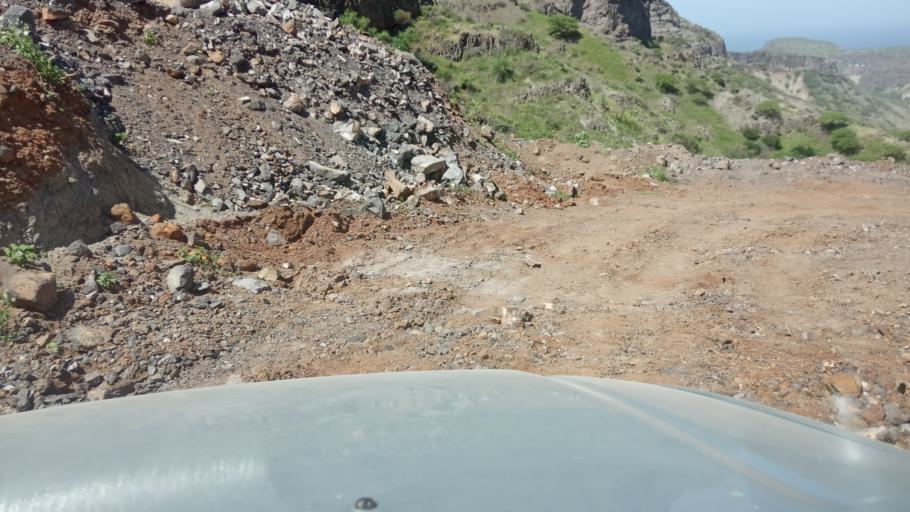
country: CV
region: Santa Catarina
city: Assomada
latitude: 15.1088
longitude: -23.7300
